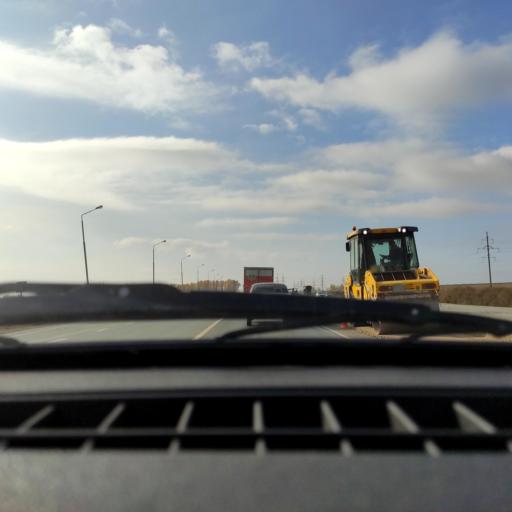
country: RU
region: Bashkortostan
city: Kabakovo
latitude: 54.6876
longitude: 56.2000
